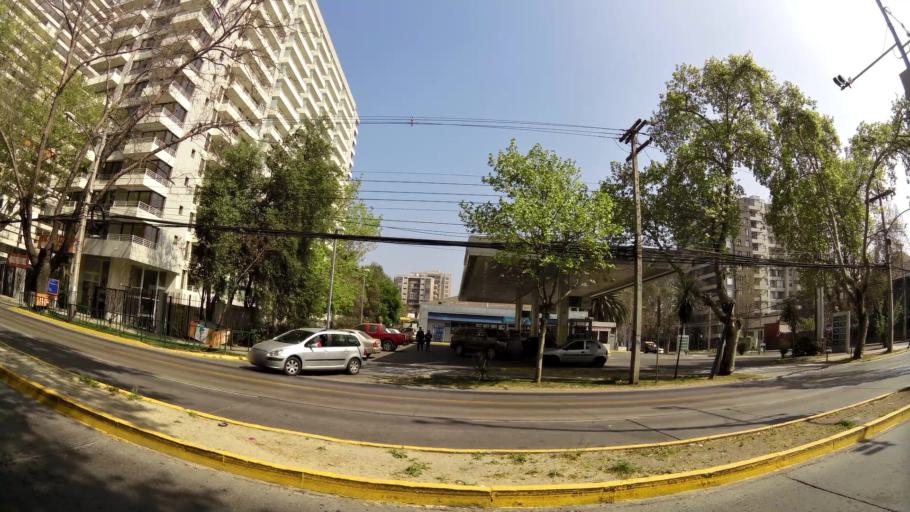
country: CL
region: Santiago Metropolitan
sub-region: Provincia de Santiago
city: Villa Presidente Frei, Nunoa, Santiago, Chile
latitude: -33.4594
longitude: -70.5980
